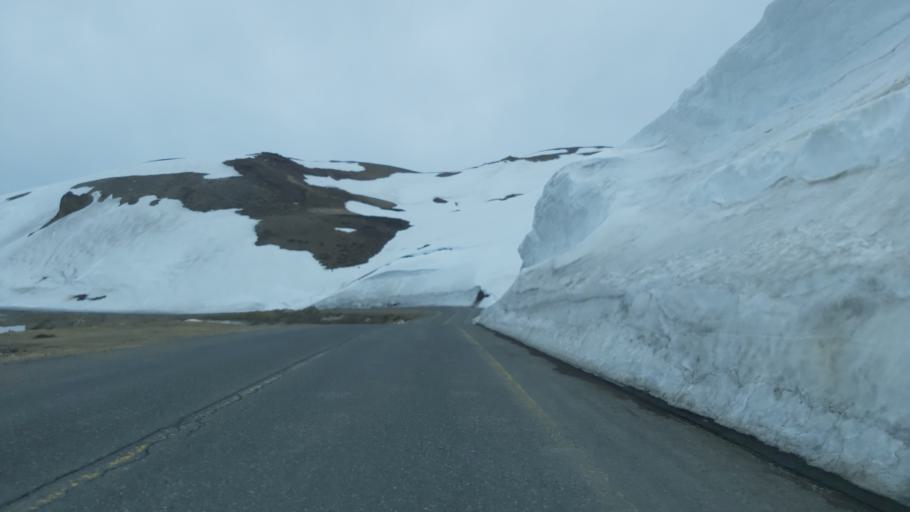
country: CL
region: Maule
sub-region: Provincia de Linares
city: Colbun
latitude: -36.0145
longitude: -70.4932
